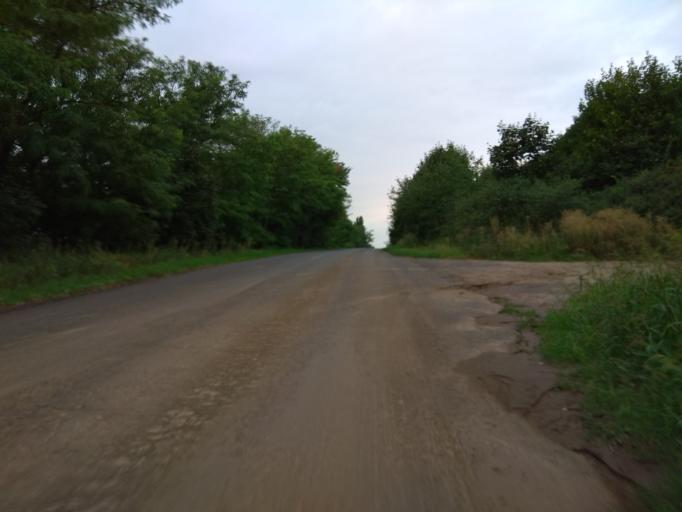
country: HU
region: Borsod-Abauj-Zemplen
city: Megyaszo
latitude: 48.1764
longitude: 21.0997
